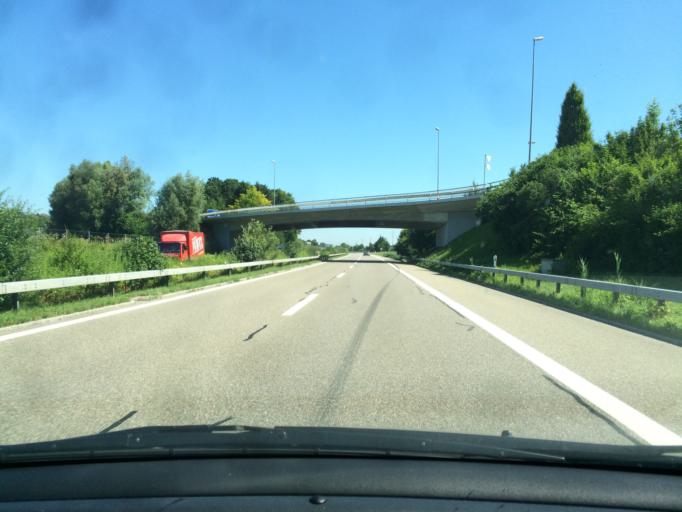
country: CH
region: Saint Gallen
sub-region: Wahlkreis Rheintal
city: Diepoldsau
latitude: 47.3907
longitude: 9.6435
